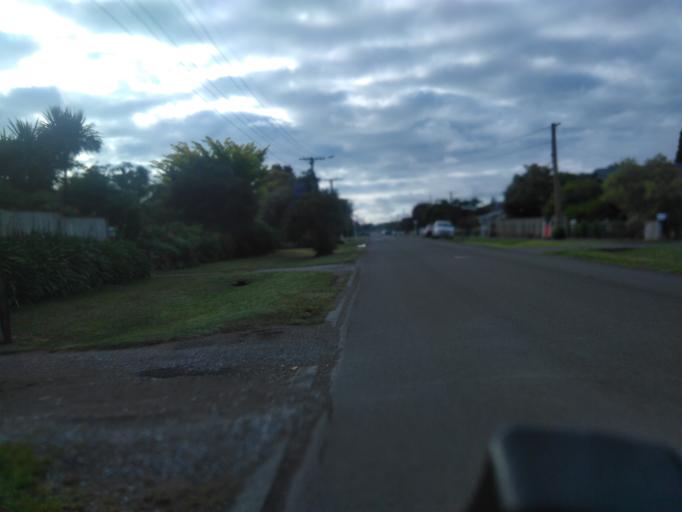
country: NZ
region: Gisborne
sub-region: Gisborne District
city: Gisborne
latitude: -38.6519
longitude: 178.0240
